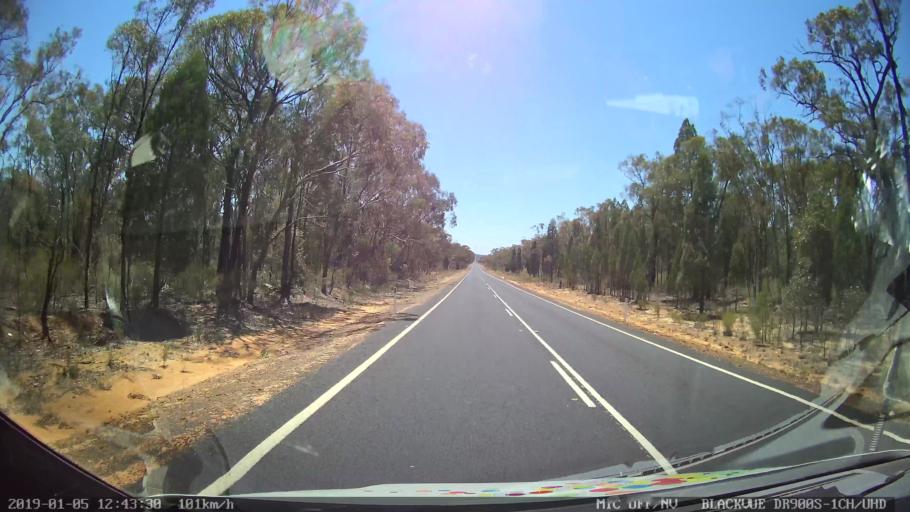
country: AU
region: New South Wales
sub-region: Warrumbungle Shire
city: Coonabarabran
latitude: -31.1475
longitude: 149.5248
